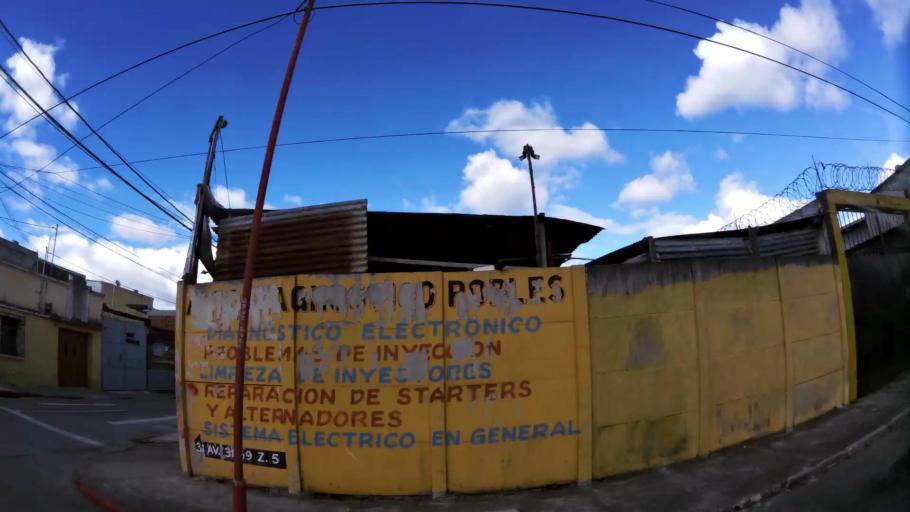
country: GT
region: Guatemala
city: Guatemala City
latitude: 14.6160
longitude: -90.5030
